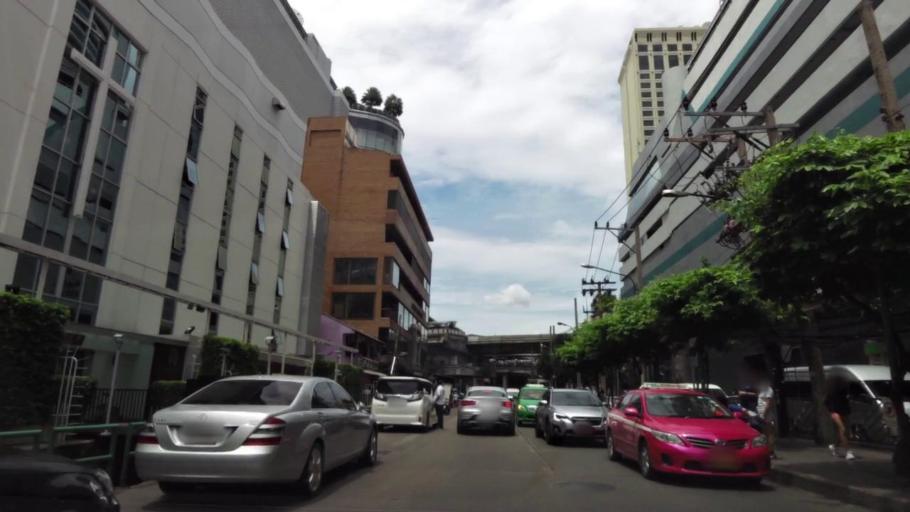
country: TH
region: Bangkok
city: Khlong Toei
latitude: 13.7385
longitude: 100.5600
